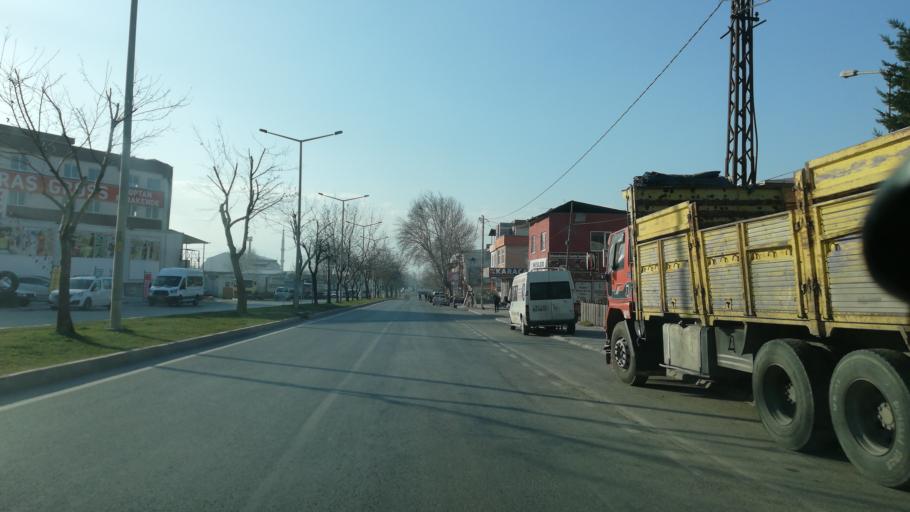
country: TR
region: Kahramanmaras
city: Kahramanmaras
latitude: 37.5648
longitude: 36.9169
